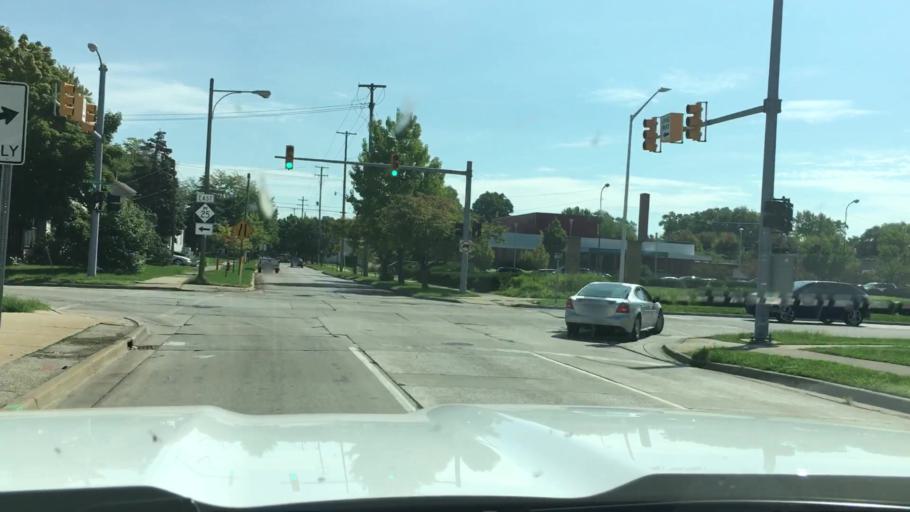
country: US
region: Michigan
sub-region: Bay County
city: Bay City
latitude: 43.5948
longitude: -83.8853
